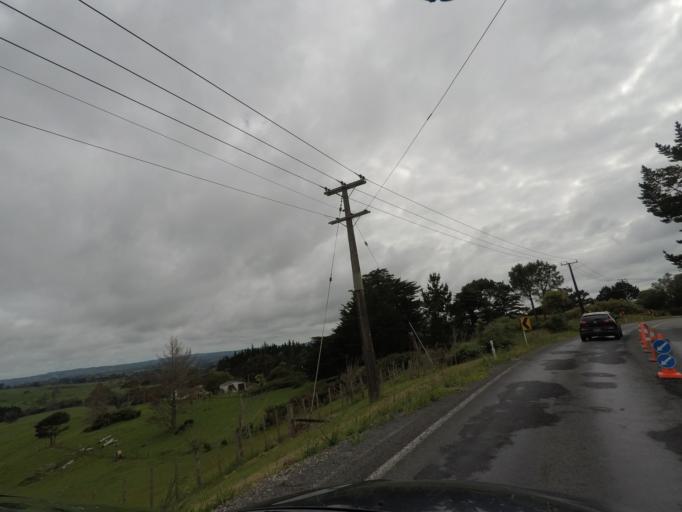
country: NZ
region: Auckland
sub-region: Auckland
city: Rosebank
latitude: -36.8365
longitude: 174.5860
